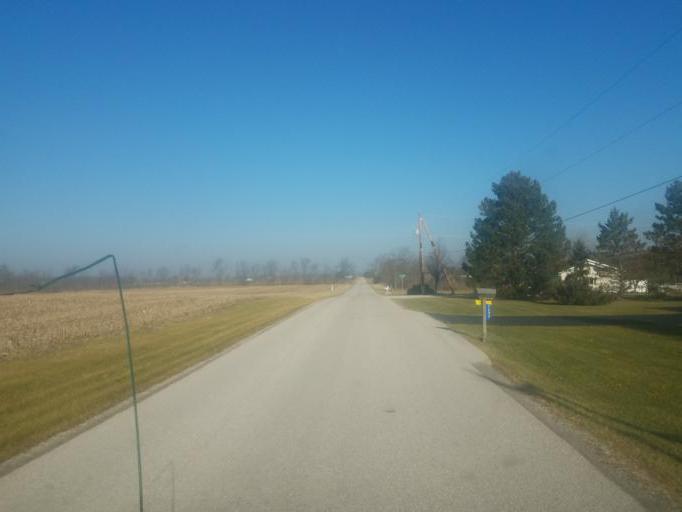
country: US
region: Ohio
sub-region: Seneca County
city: Tiffin
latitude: 41.0852
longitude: -83.1122
